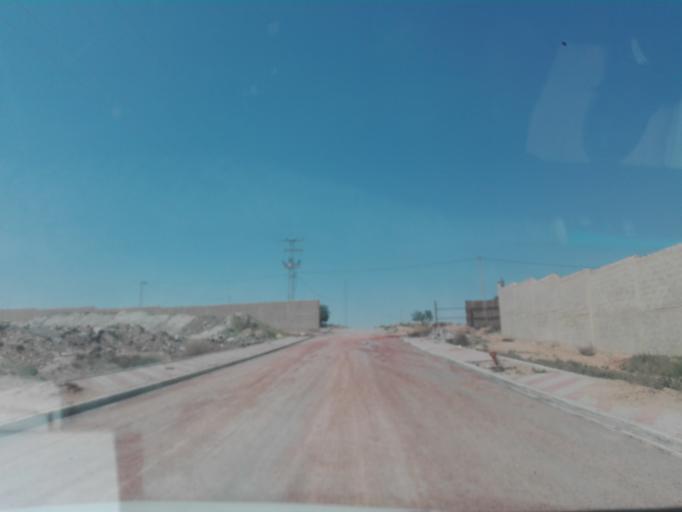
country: TN
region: Safaqis
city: Sfax
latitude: 34.7214
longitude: 10.5188
